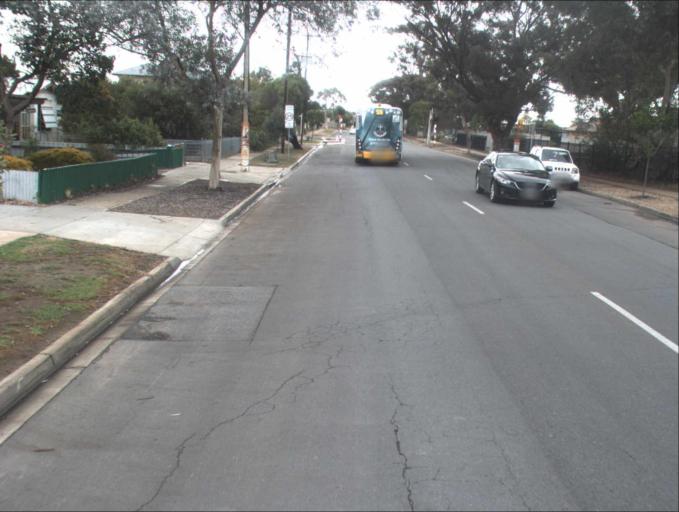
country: AU
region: South Australia
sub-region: Port Adelaide Enfield
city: Gilles Plains
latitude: -34.8498
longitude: 138.6611
